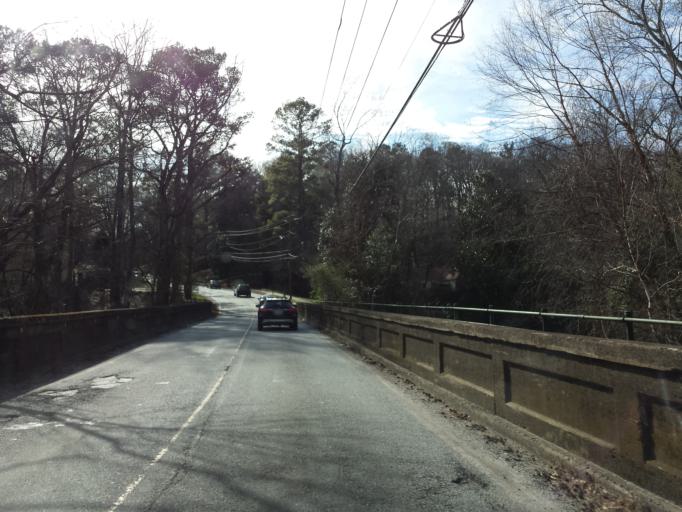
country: US
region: Georgia
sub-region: Cobb County
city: Vinings
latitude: 33.8264
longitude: -84.4425
